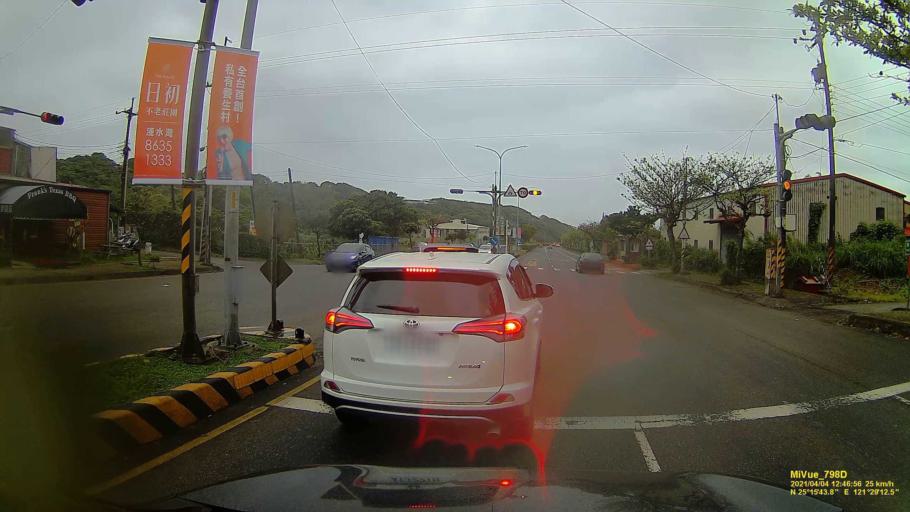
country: TW
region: Taipei
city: Taipei
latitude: 25.2622
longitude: 121.4867
